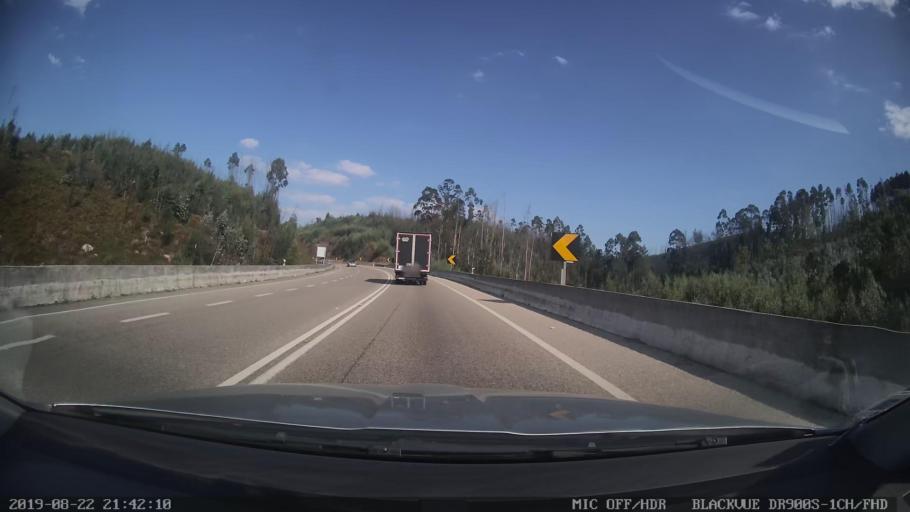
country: PT
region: Leiria
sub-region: Figueiro Dos Vinhos
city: Figueiro dos Vinhos
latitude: 39.9307
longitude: -8.3367
